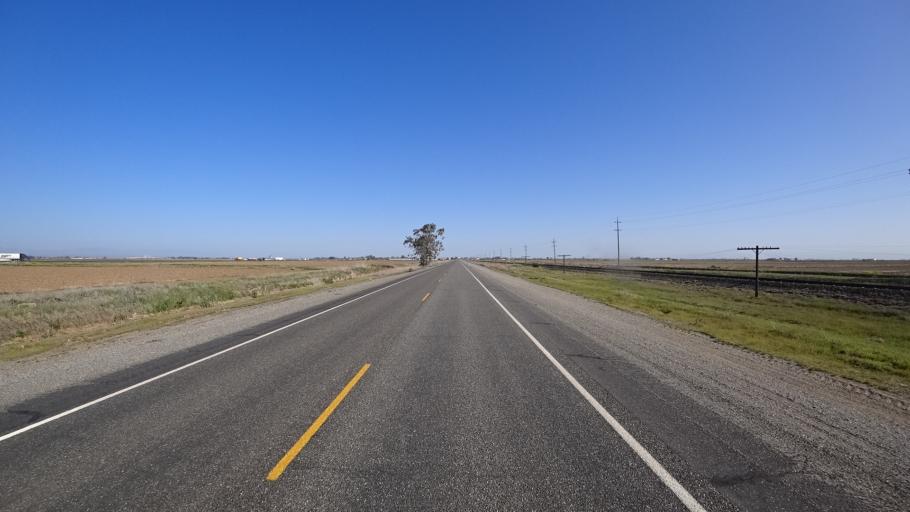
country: US
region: California
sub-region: Glenn County
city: Willows
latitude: 39.4815
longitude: -122.1931
